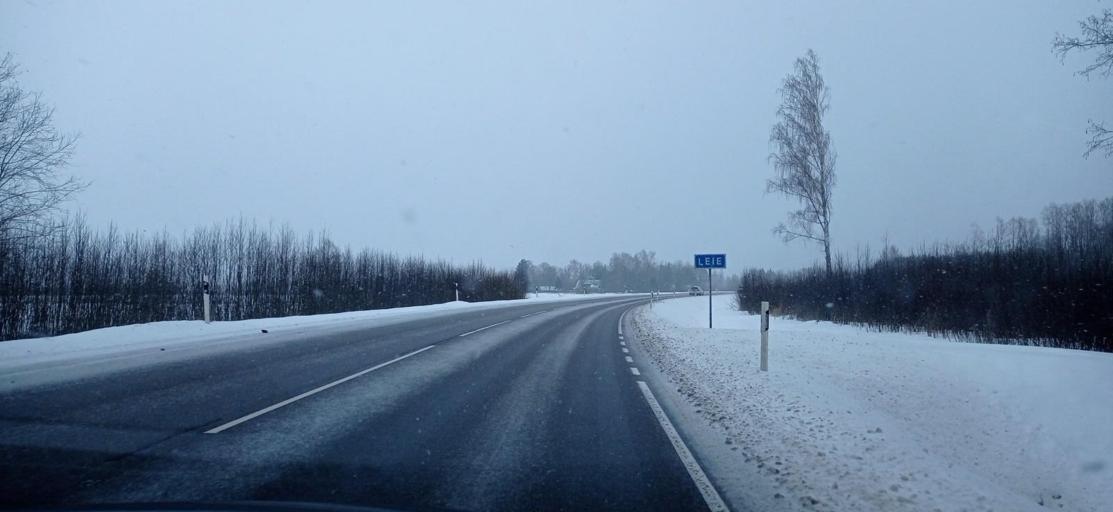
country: EE
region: Jogevamaa
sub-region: Poltsamaa linn
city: Poltsamaa
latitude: 58.4137
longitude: 26.0114
